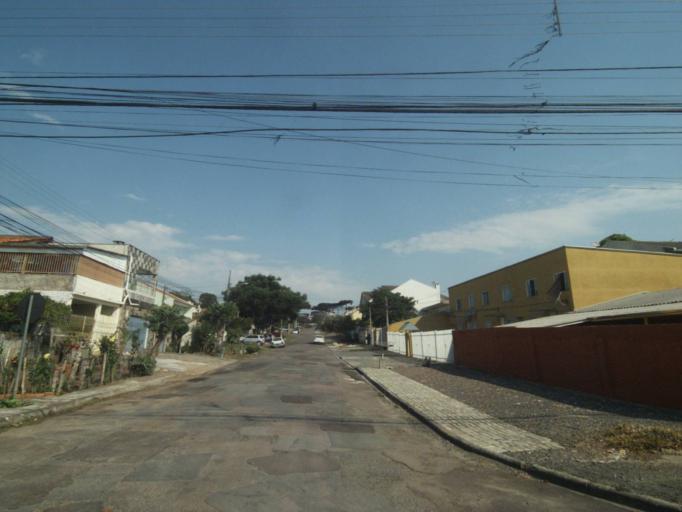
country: BR
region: Parana
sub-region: Sao Jose Dos Pinhais
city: Sao Jose dos Pinhais
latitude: -25.5083
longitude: -49.2594
